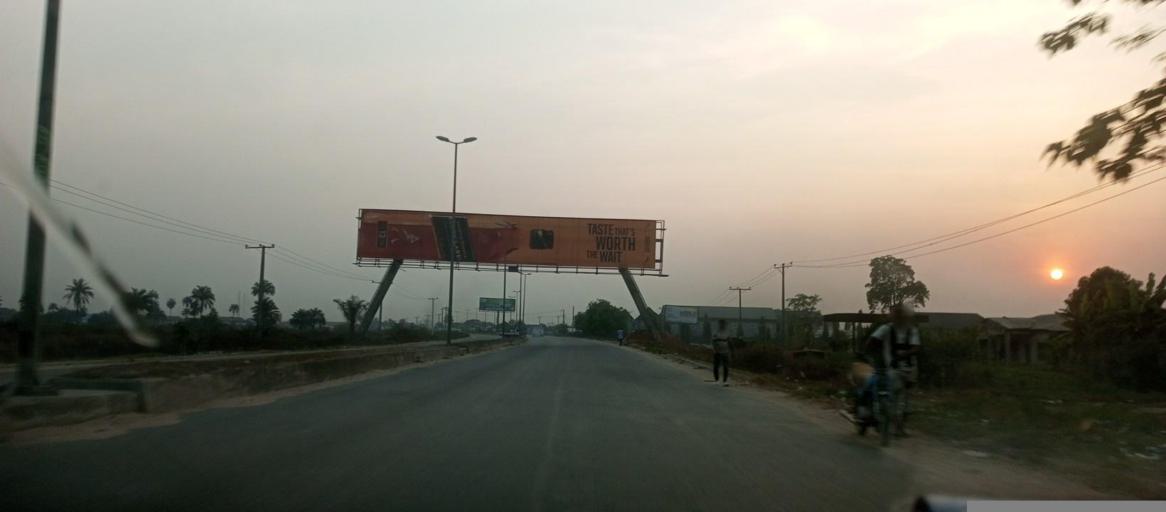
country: NG
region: Rivers
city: Emuoha
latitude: 4.9291
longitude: 7.0006
